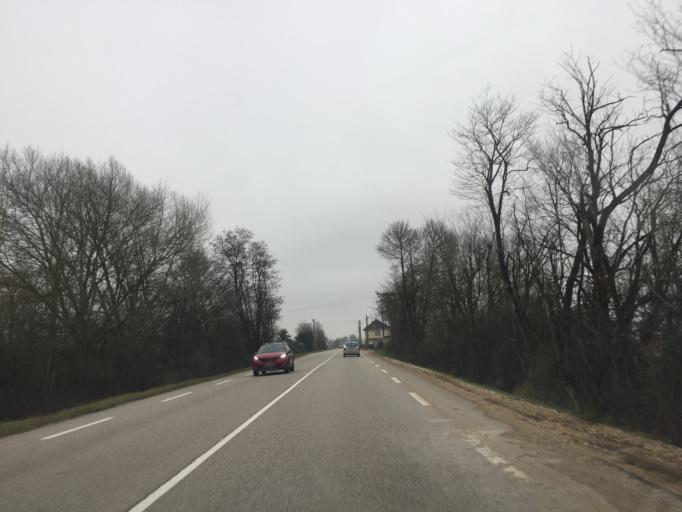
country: FR
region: Rhone-Alpes
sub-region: Departement de l'Ain
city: Ambronay
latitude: 46.0171
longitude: 5.3399
